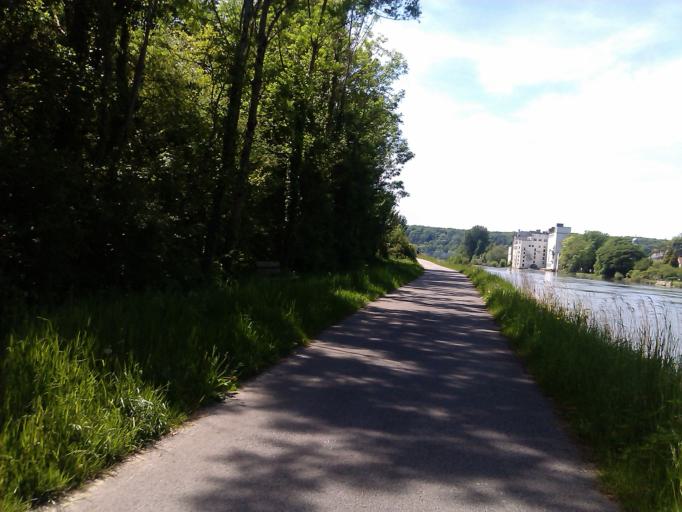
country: FR
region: Franche-Comte
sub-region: Departement du Doubs
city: Avanne-Aveney
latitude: 47.1992
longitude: 5.9721
